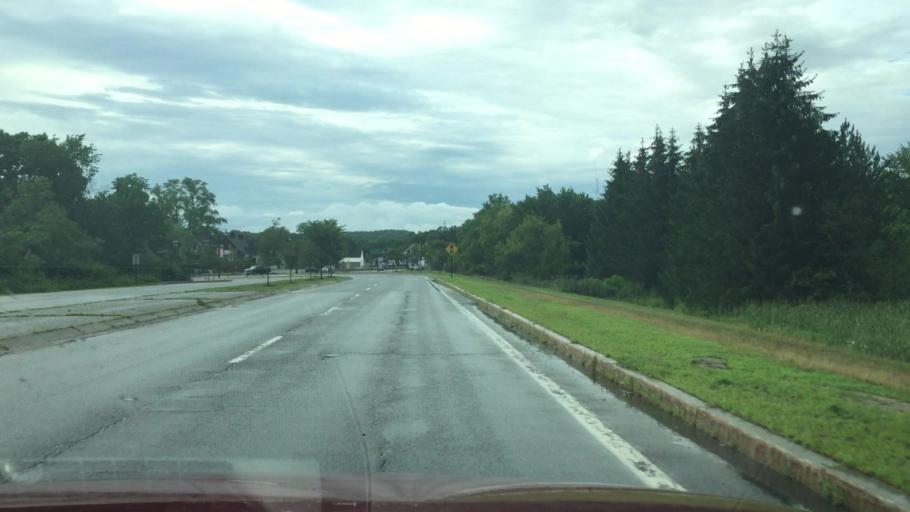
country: US
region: Maine
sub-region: Cumberland County
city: Westbrook
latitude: 43.6766
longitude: -70.3531
